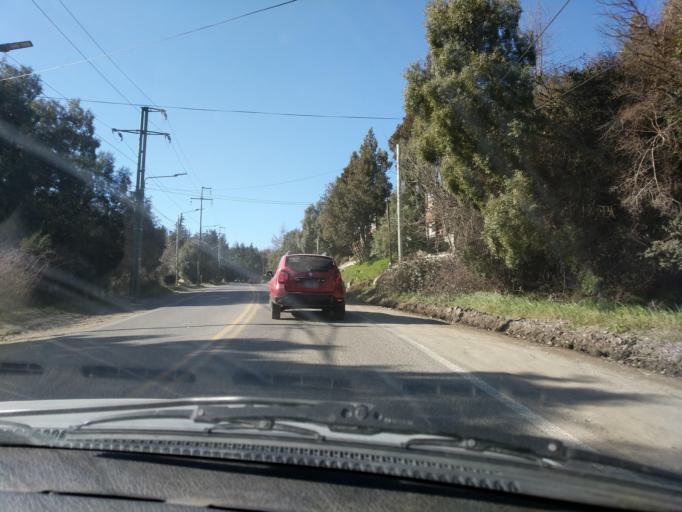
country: AR
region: Rio Negro
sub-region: Departamento de Bariloche
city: San Carlos de Bariloche
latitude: -41.1269
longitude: -71.3910
